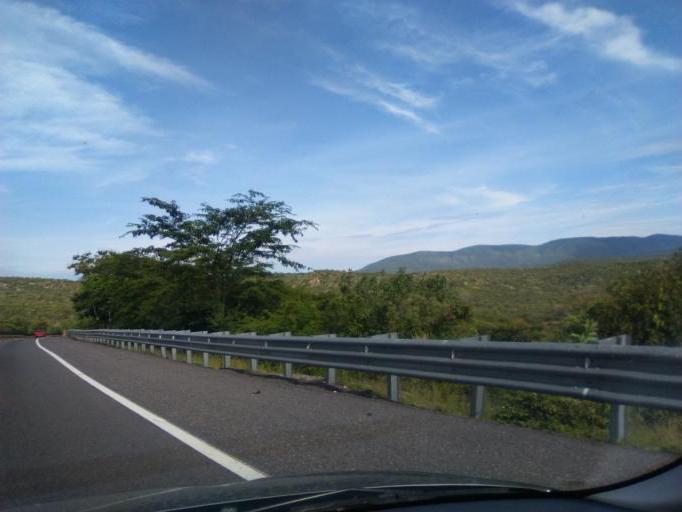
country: MX
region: Guerrero
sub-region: Huitzuco de los Figueroa
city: San Francisco Ozomatlan
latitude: 17.9908
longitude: -99.3102
